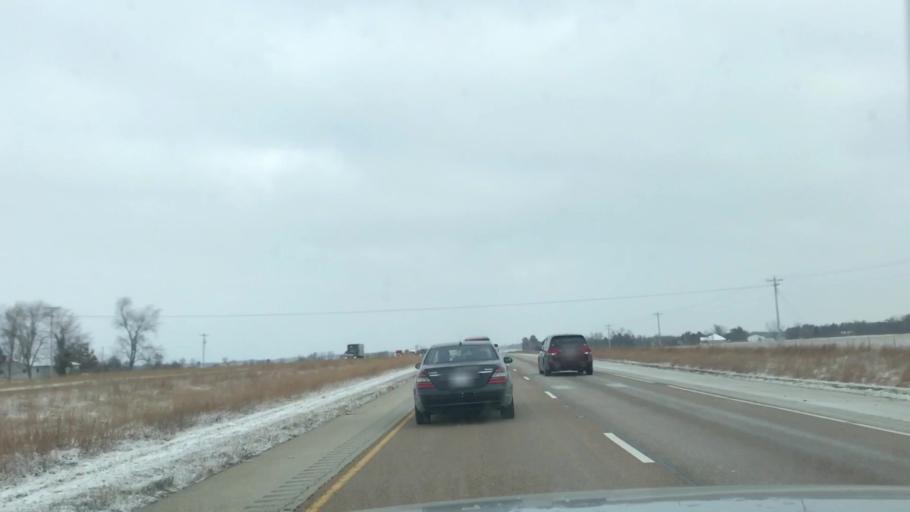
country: US
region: Illinois
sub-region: Montgomery County
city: Litchfield
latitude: 39.2400
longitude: -89.6411
